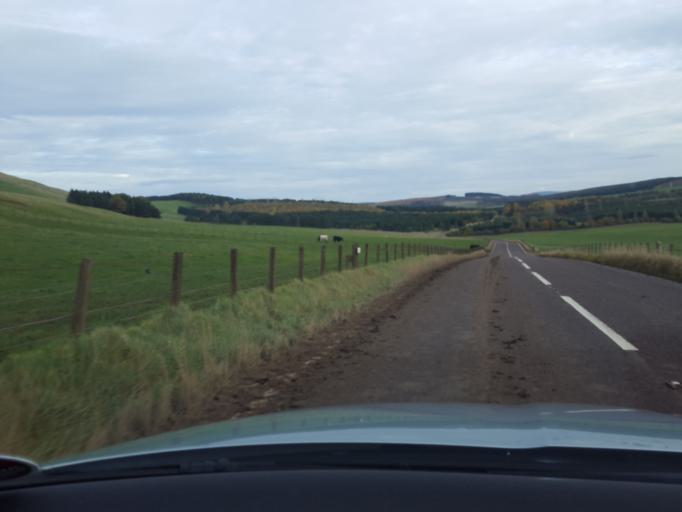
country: GB
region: Scotland
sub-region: South Lanarkshire
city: Biggar
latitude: 55.6816
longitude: -3.4761
